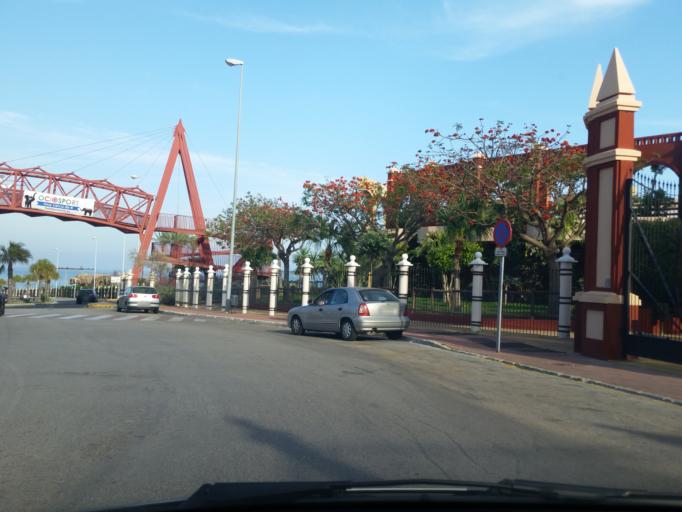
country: ES
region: Andalusia
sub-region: Provincia de Malaga
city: Benalmadena
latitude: 36.5751
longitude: -4.5817
